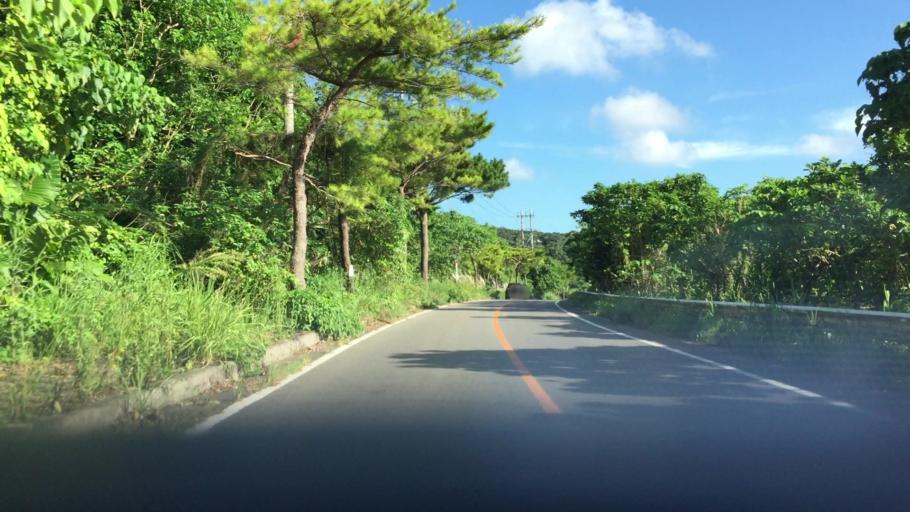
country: JP
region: Okinawa
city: Ishigaki
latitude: 24.3830
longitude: 124.1531
